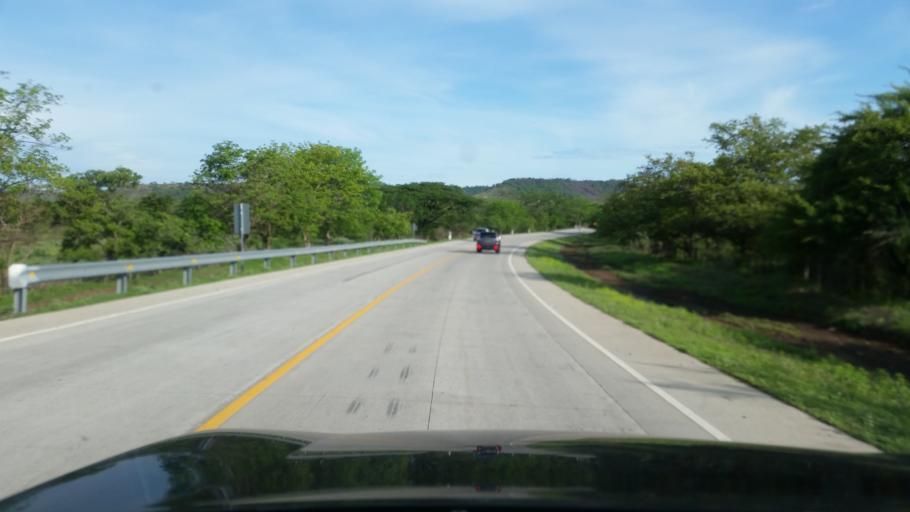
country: NI
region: Leon
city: Nagarote
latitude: 12.1335
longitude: -86.6457
